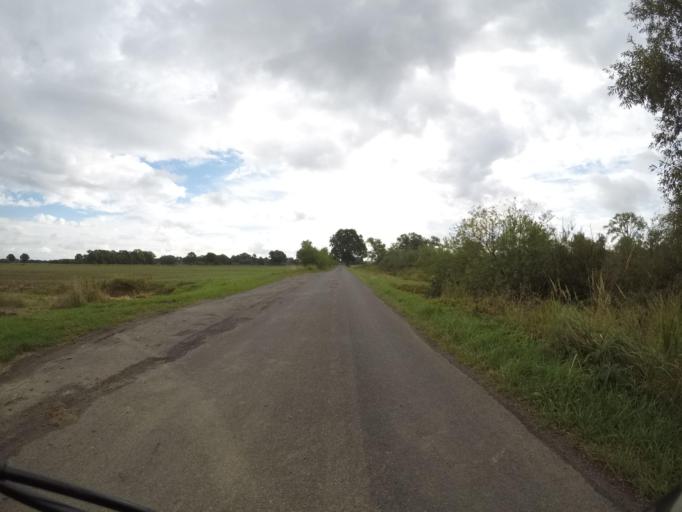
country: DE
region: Lower Saxony
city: Neu Darchau
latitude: 53.2656
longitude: 10.8413
